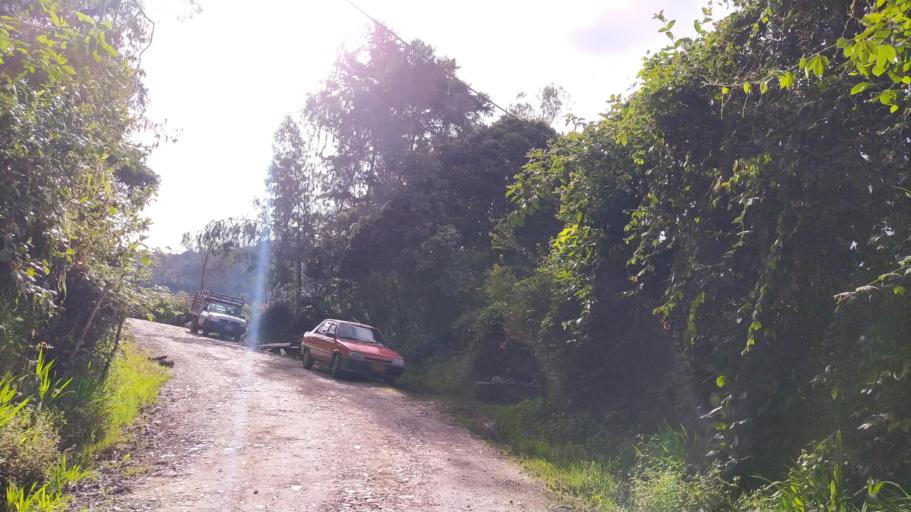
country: CO
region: Cundinamarca
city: Tenza
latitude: 5.0908
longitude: -73.4759
